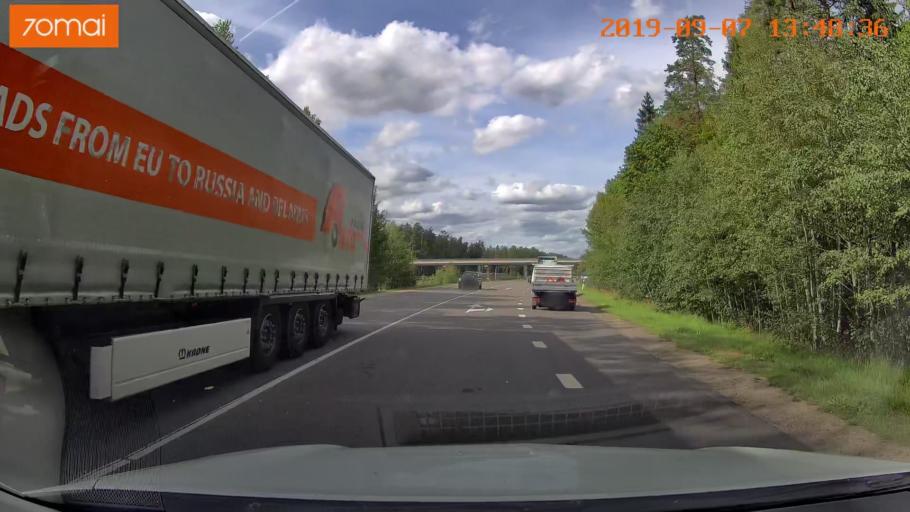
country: LT
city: Baltoji Voke
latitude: 54.6025
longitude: 25.2007
